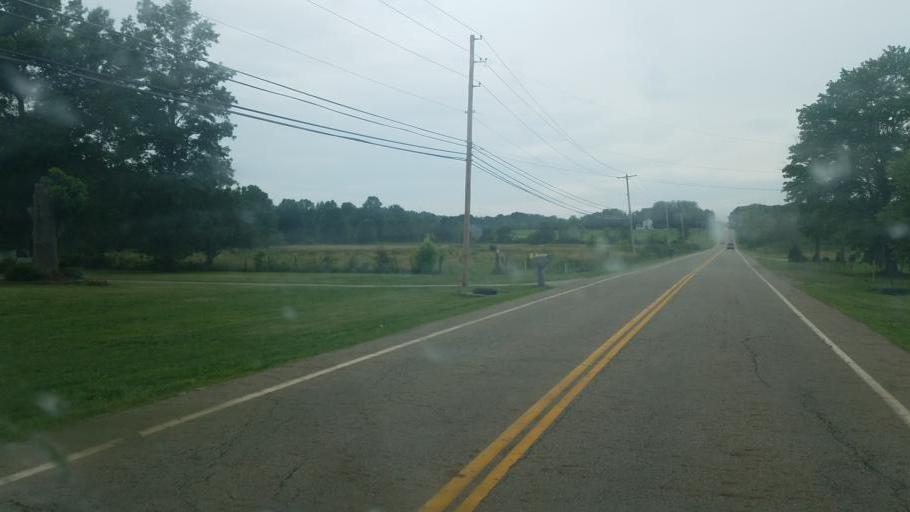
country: US
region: Ohio
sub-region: Summit County
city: Manchester
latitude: 40.9321
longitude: -81.5927
